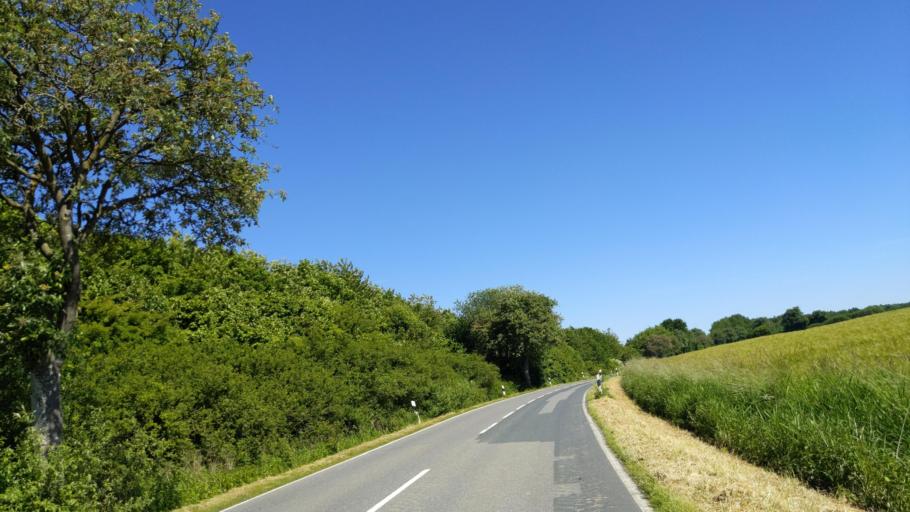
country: DE
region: Schleswig-Holstein
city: Altenkrempe
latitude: 54.1433
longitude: 10.8462
